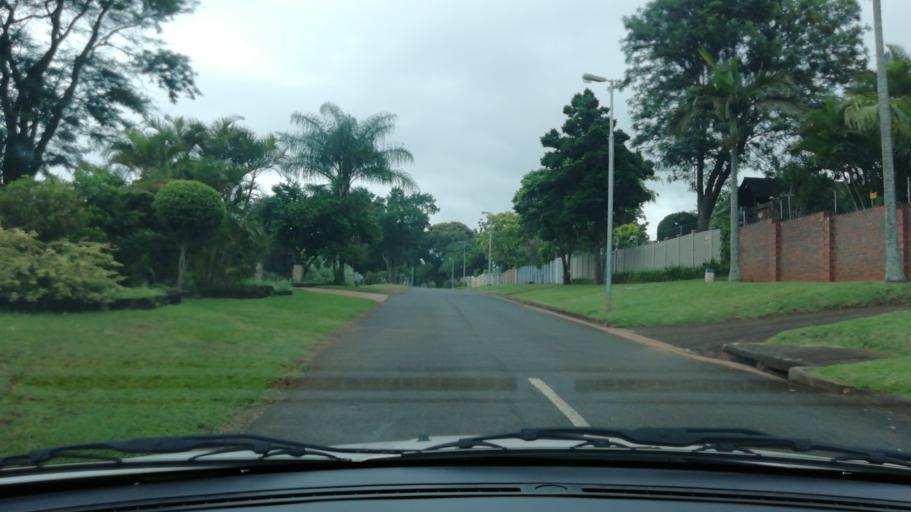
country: ZA
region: KwaZulu-Natal
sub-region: uThungulu District Municipality
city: Empangeni
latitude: -28.7610
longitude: 31.8954
